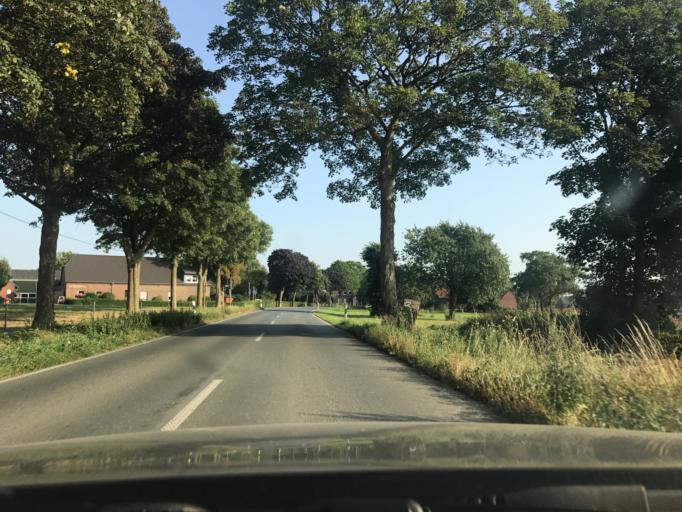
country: DE
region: North Rhine-Westphalia
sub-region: Regierungsbezirk Dusseldorf
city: Goch
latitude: 51.7418
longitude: 6.1979
